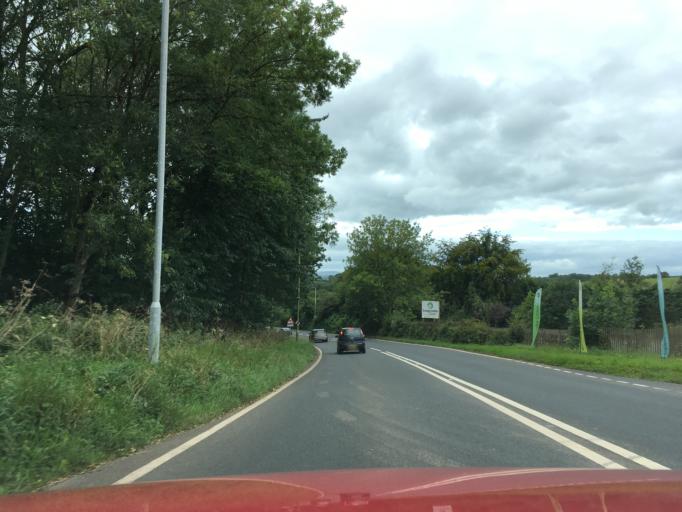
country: GB
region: England
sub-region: Devon
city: Totnes
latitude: 50.4296
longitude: -3.6441
